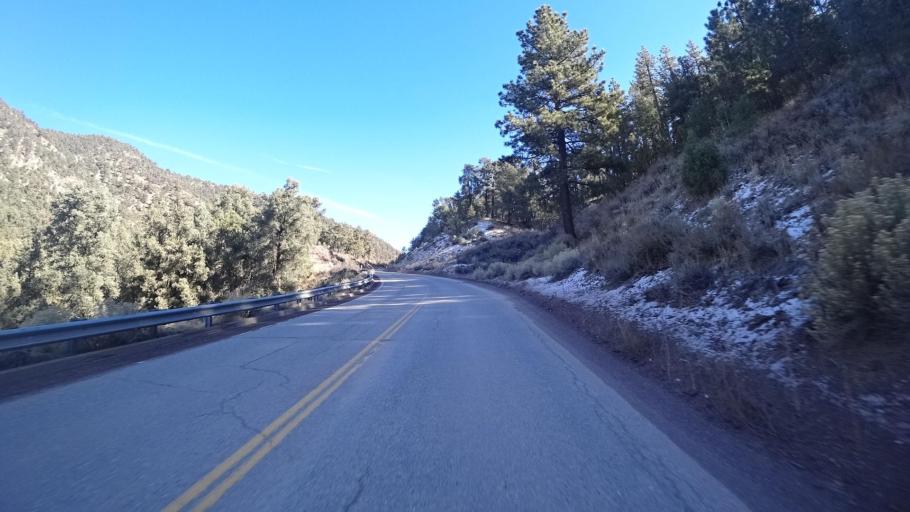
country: US
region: California
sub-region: Kern County
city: Pine Mountain Club
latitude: 34.8516
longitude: -119.1139
